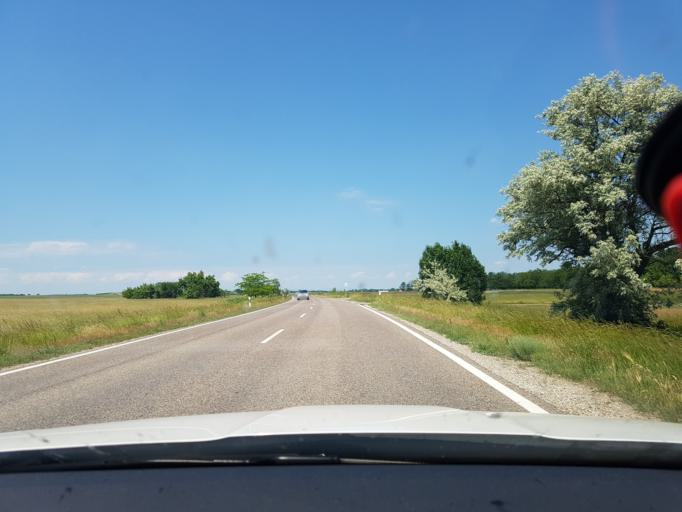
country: HU
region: Hajdu-Bihar
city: Egyek
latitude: 47.5693
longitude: 20.8606
